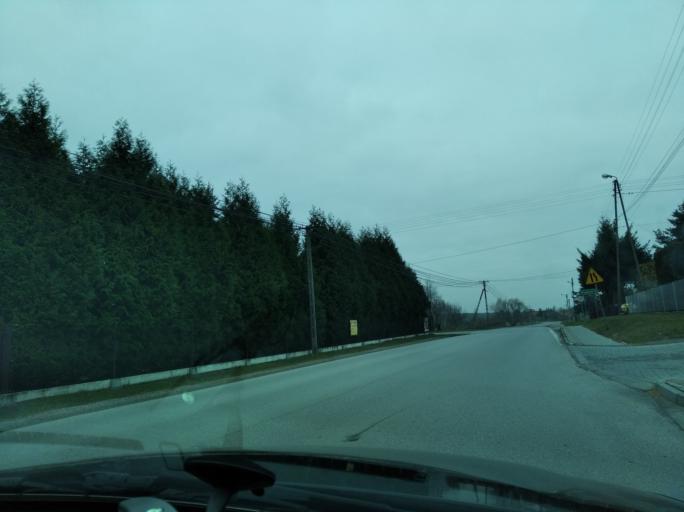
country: PL
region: Subcarpathian Voivodeship
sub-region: Powiat lancucki
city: Rakszawa
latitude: 50.1600
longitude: 22.2390
